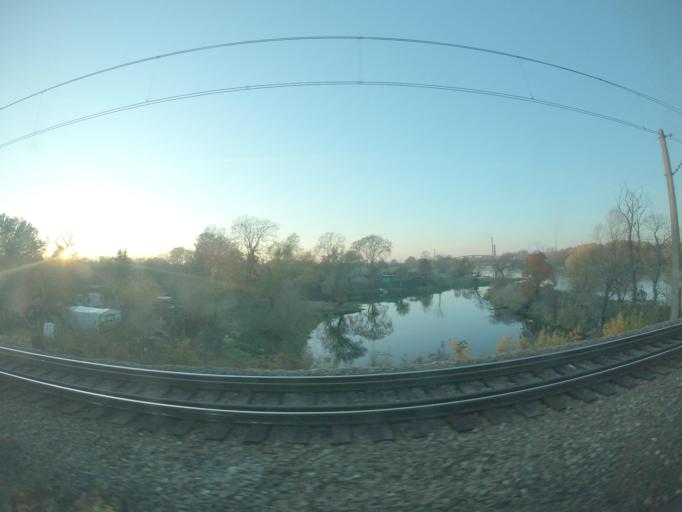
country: PL
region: Lubusz
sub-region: Powiat gorzowski
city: Kostrzyn nad Odra
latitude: 52.5835
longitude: 14.6430
